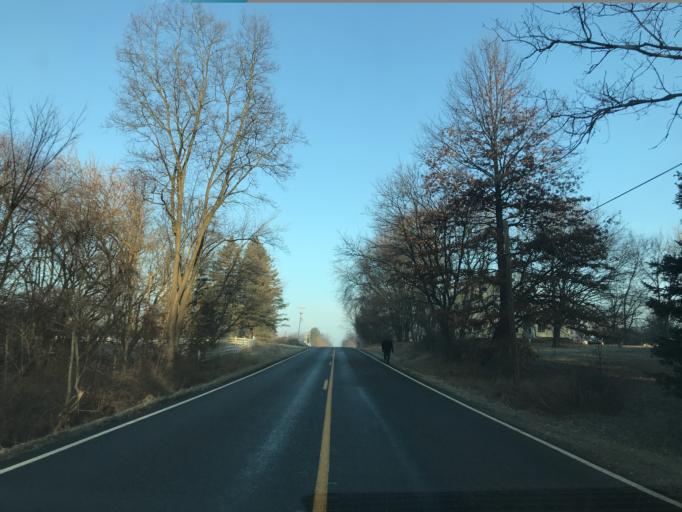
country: US
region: Michigan
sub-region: Ingham County
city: Leslie
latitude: 42.3883
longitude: -84.4574
